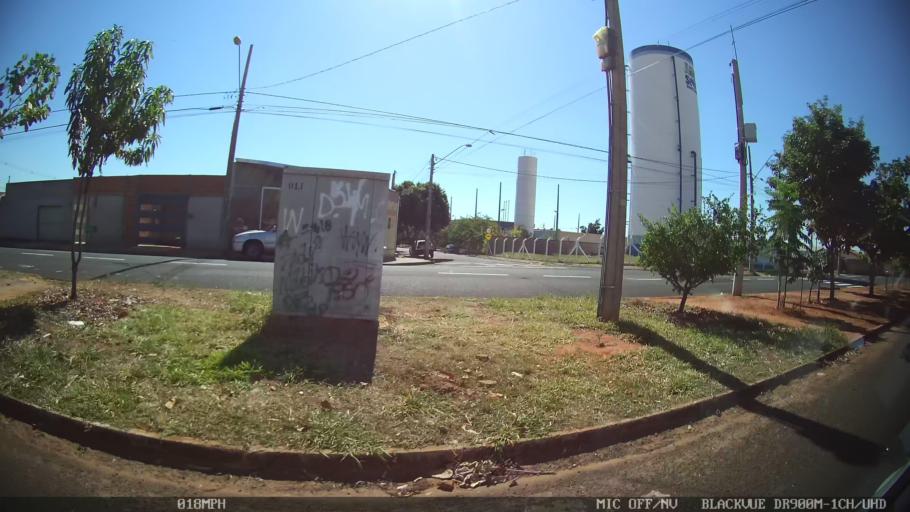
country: BR
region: Sao Paulo
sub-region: Sao Jose Do Rio Preto
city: Sao Jose do Rio Preto
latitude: -20.7405
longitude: -49.4162
